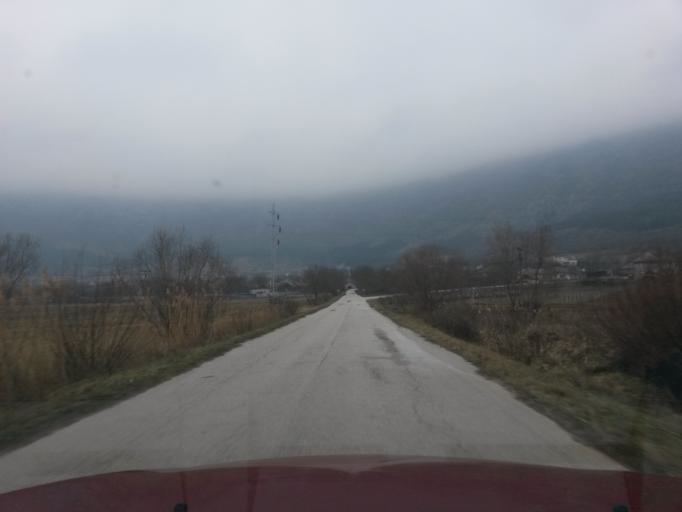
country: SK
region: Kosicky
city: Medzev
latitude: 48.6019
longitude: 20.7585
